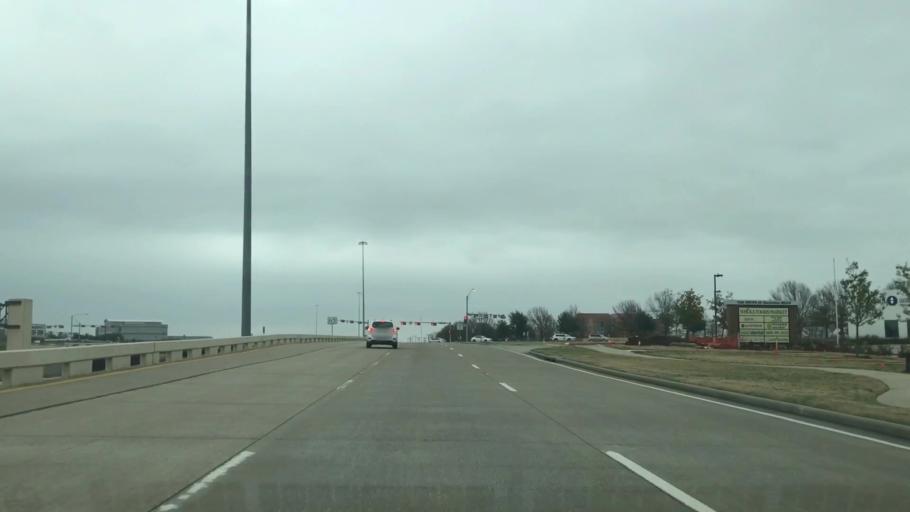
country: US
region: Texas
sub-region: Dallas County
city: Farmers Branch
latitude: 32.9028
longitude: -96.9605
